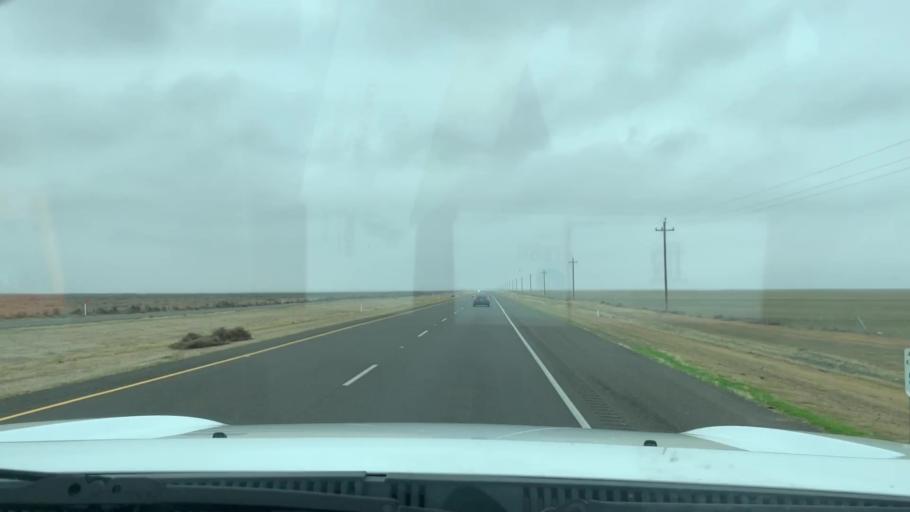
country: US
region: California
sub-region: Kern County
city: Lost Hills
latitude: 35.6160
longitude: -119.7707
